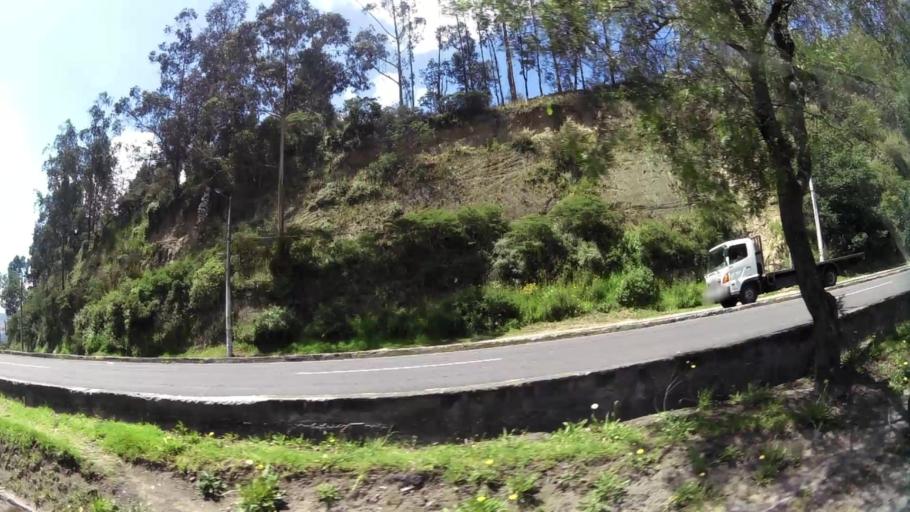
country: EC
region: Pichincha
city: Quito
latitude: -0.0971
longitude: -78.4688
